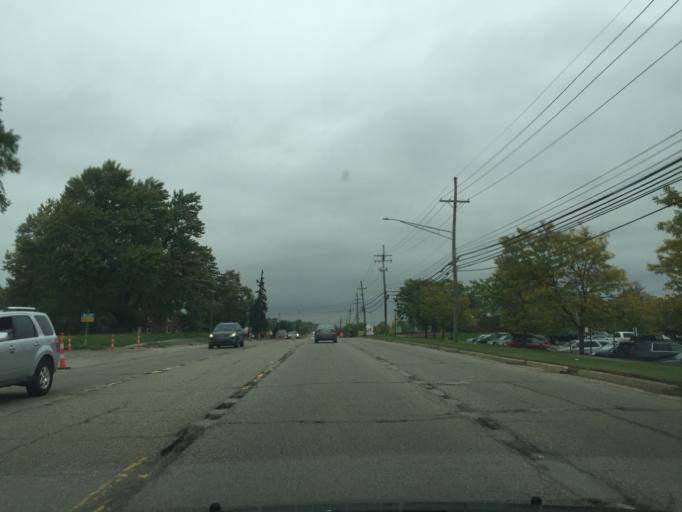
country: US
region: Michigan
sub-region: Oakland County
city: Auburn Hills
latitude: 42.6668
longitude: -83.2457
